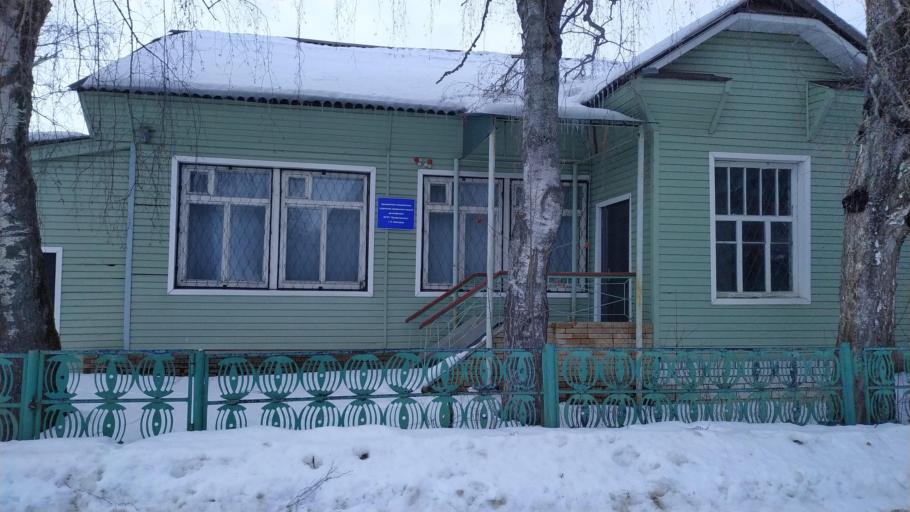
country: RU
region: Nizjnij Novgorod
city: Vyyezdnoye
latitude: 55.3924
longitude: 43.8102
